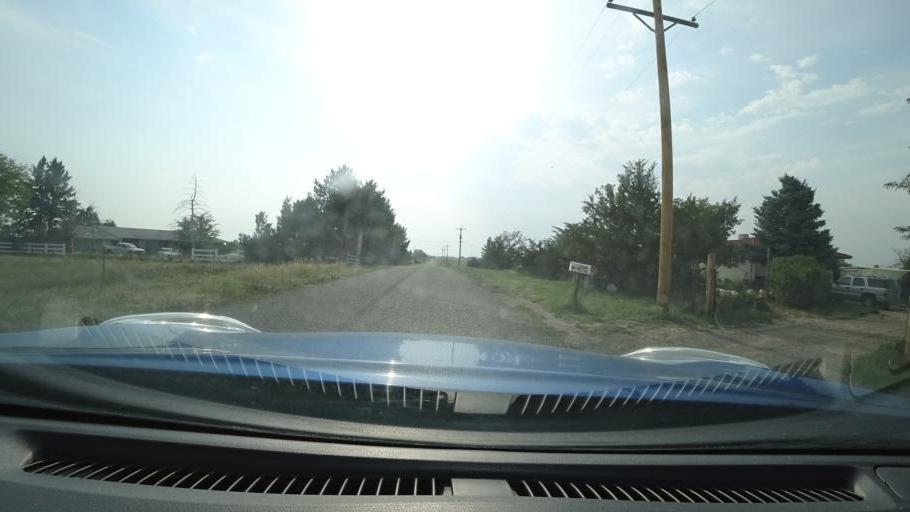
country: US
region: Colorado
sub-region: Adams County
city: Aurora
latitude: 39.7256
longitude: -104.7361
